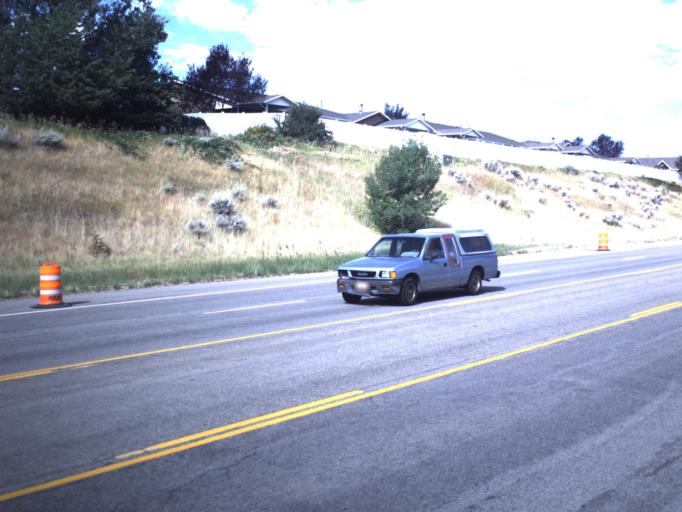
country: US
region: Utah
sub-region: Weber County
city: Washington Terrace
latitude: 41.1616
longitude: -111.9485
